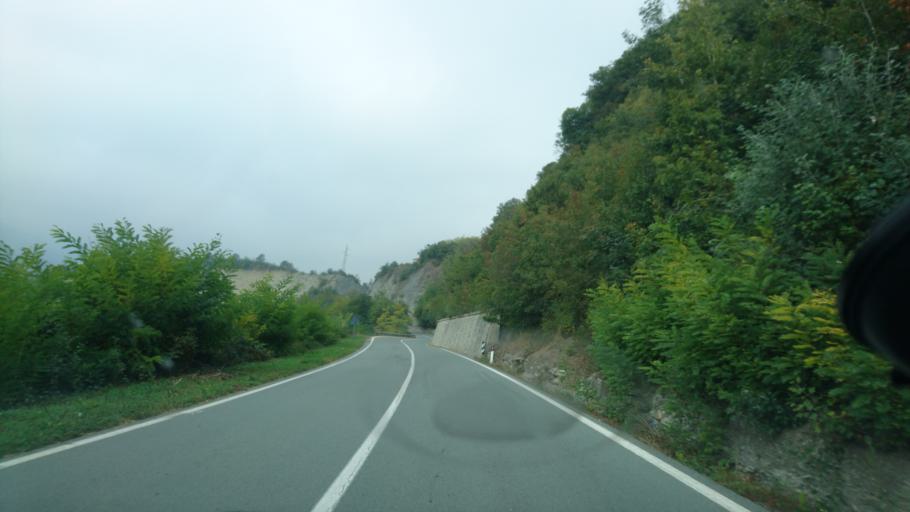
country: IT
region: Piedmont
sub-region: Provincia di Asti
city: Mombaldone
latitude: 44.5731
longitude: 8.3515
